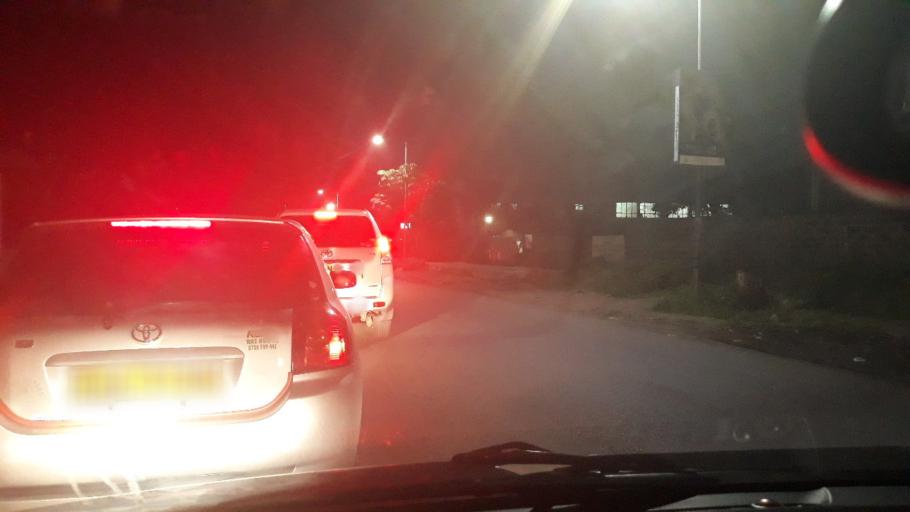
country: KE
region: Nairobi Area
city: Pumwani
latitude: -1.2960
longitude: 36.8350
